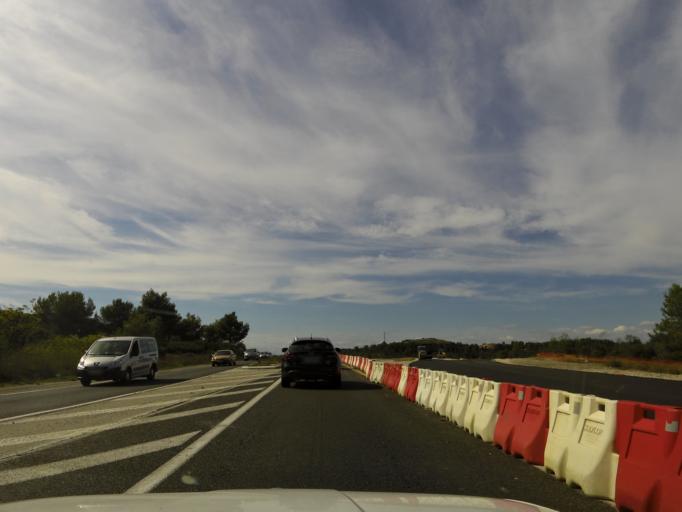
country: FR
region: Languedoc-Roussillon
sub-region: Departement du Gard
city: La Calmette
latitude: 43.9010
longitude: 4.2863
